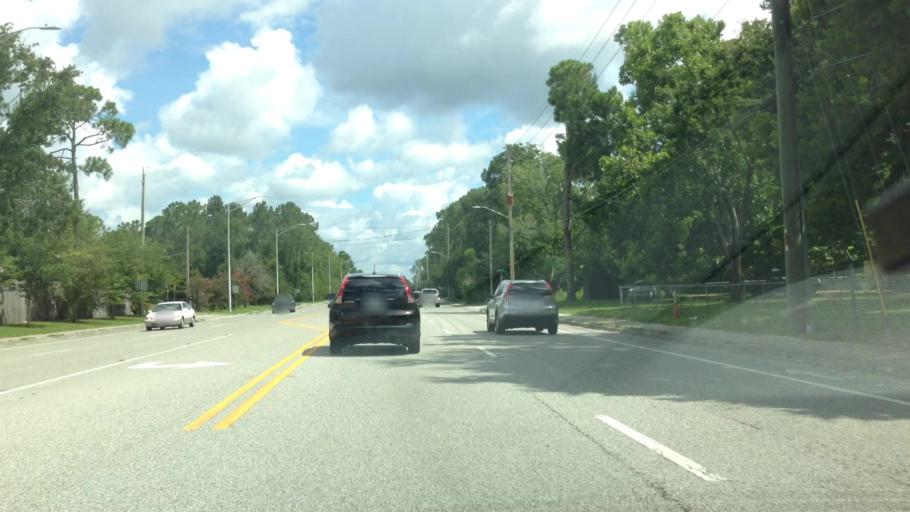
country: US
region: Florida
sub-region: Duval County
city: Neptune Beach
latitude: 30.2918
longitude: -81.4589
